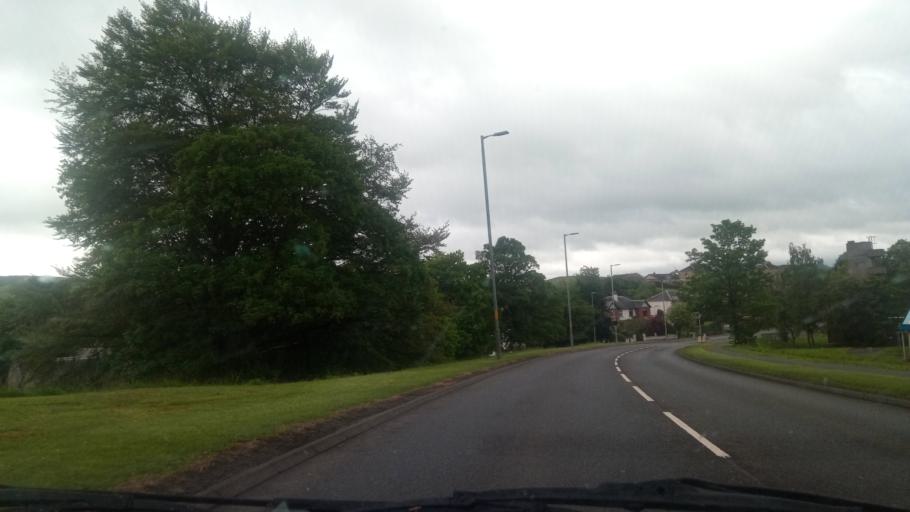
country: GB
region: Scotland
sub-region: The Scottish Borders
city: Hawick
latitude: 55.4337
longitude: -2.7798
